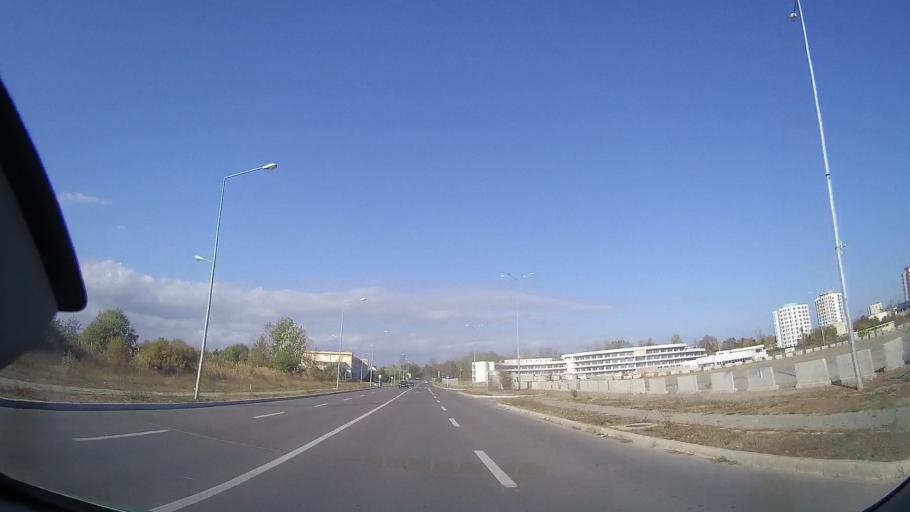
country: RO
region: Constanta
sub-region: Municipiul Mangalia
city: Mangalia
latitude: 43.8420
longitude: 28.5897
